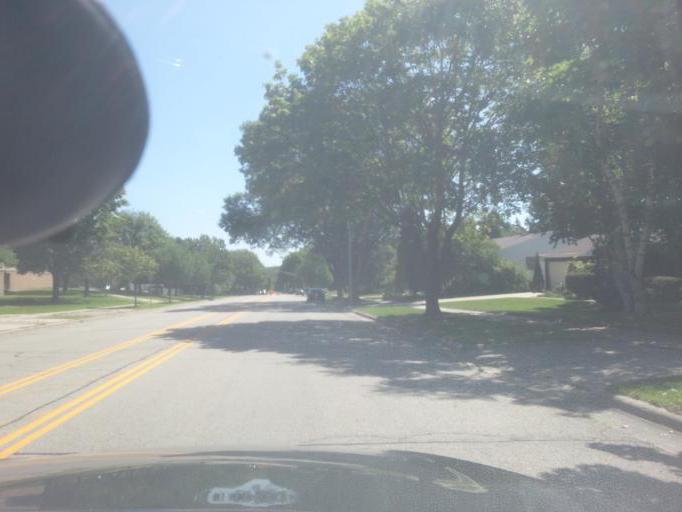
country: US
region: Wisconsin
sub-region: Dane County
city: Middleton
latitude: 43.0675
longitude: -89.4954
